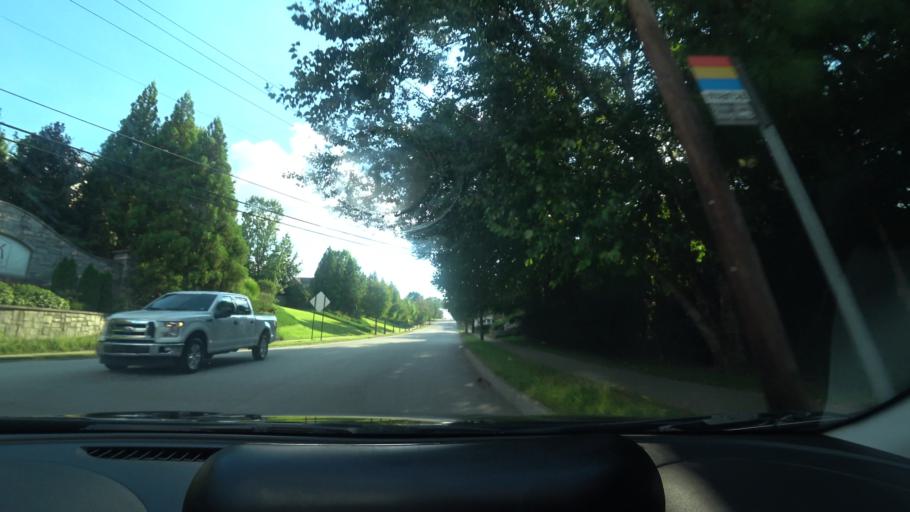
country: US
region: Georgia
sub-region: Fulton County
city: Atlanta
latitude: 33.7087
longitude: -84.3942
